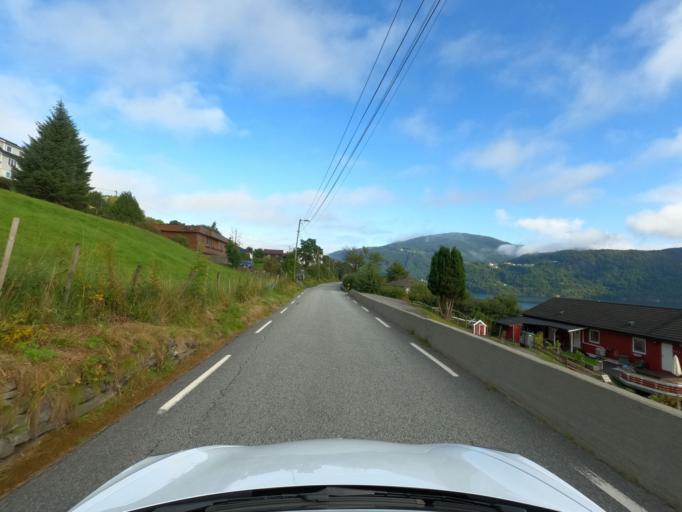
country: NO
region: Hordaland
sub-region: Bergen
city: Indre Arna
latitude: 60.4296
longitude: 5.4987
